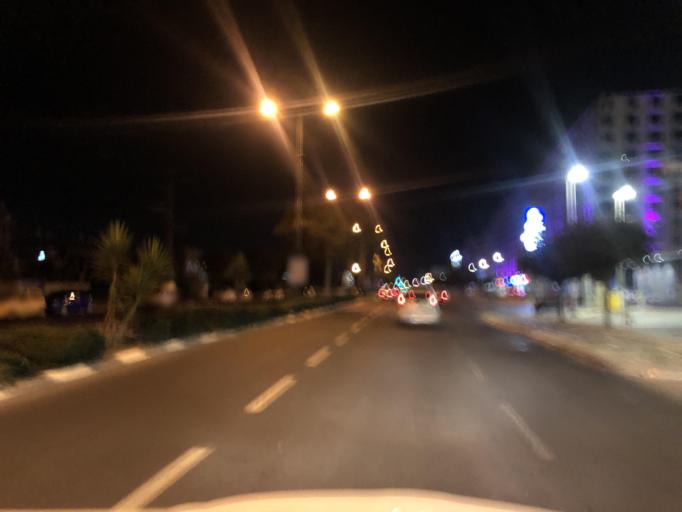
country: IL
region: Tel Aviv
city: Yafo
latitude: 32.0485
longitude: 34.7760
